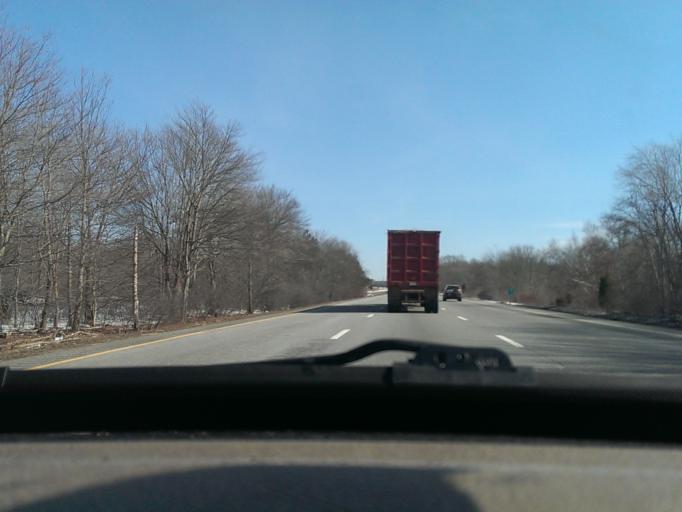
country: US
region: Massachusetts
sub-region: Bristol County
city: Seekonk
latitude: 41.7865
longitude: -71.2979
